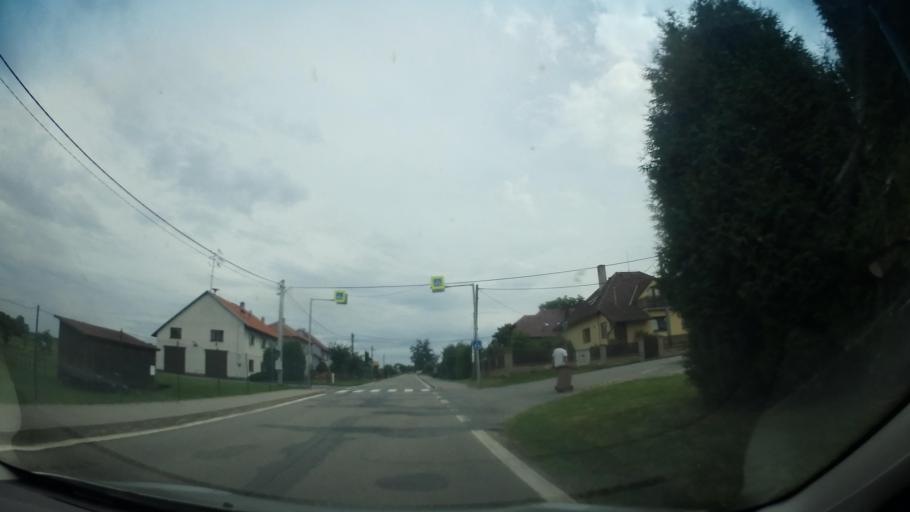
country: CZ
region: Vysocina
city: Bystrice nad Pernstejnem
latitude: 49.4928
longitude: 16.1788
